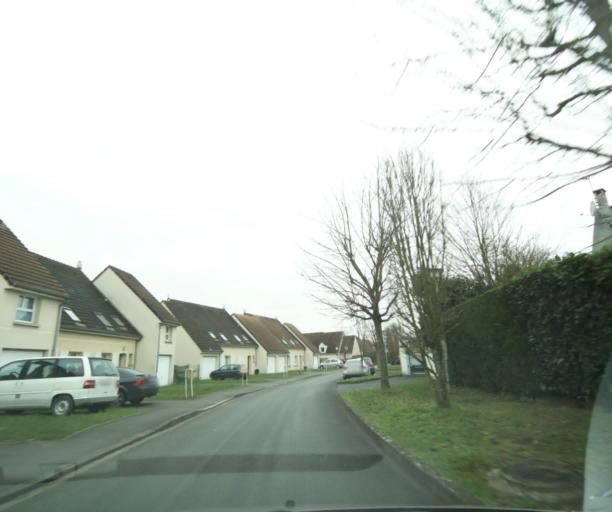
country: FR
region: Picardie
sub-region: Departement de l'Oise
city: Noyon
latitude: 49.5741
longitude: 2.9936
